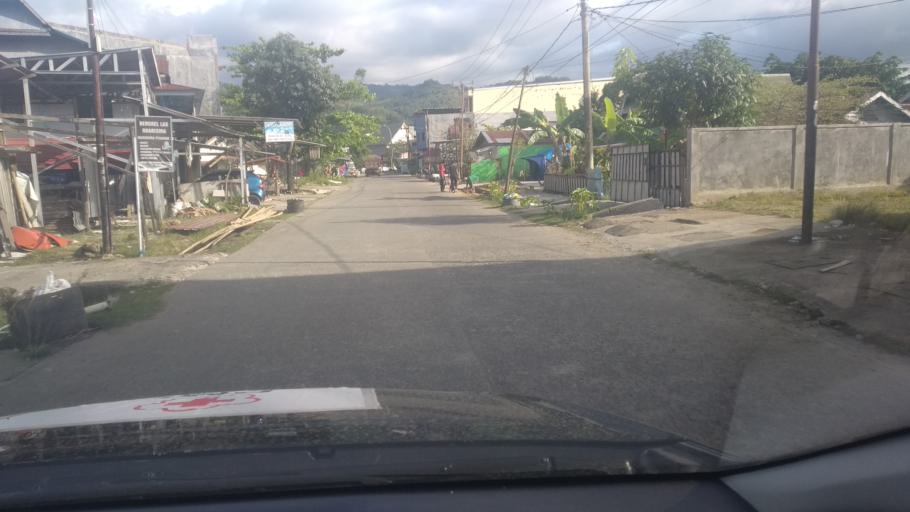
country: ID
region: Sulawesi Barat
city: Mamuju
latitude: -2.6796
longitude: 118.8861
